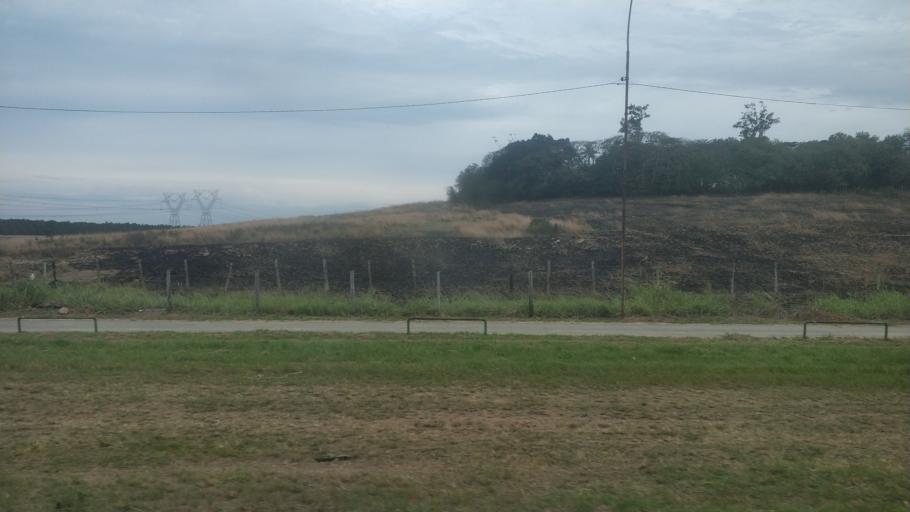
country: BR
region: Rio de Janeiro
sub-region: Seropedica
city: Seropedica
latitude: -22.7828
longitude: -43.6583
